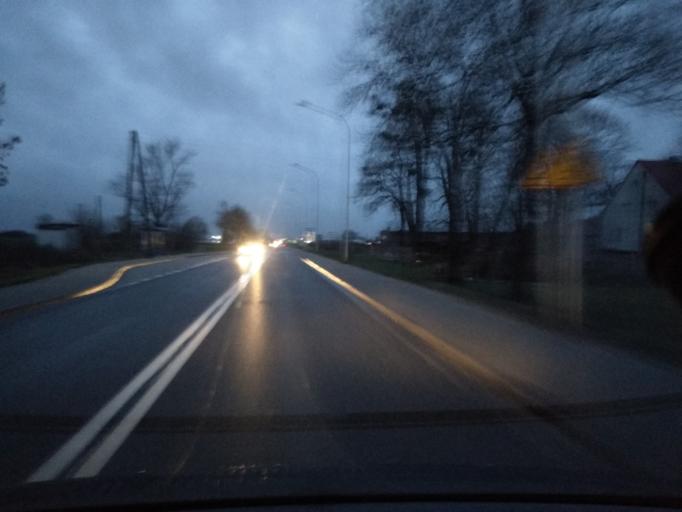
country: PL
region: Lower Silesian Voivodeship
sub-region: Powiat sredzki
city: Miekinia
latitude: 51.1586
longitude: 16.7503
